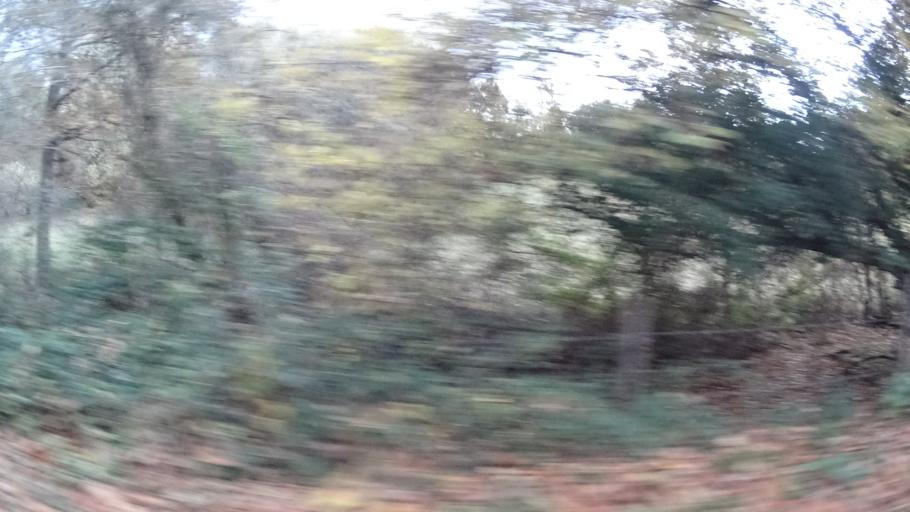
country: FR
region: Pays de la Loire
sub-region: Departement de la Loire-Atlantique
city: Saint-Nicolas-de-Redon
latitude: 47.6640
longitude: -2.0529
